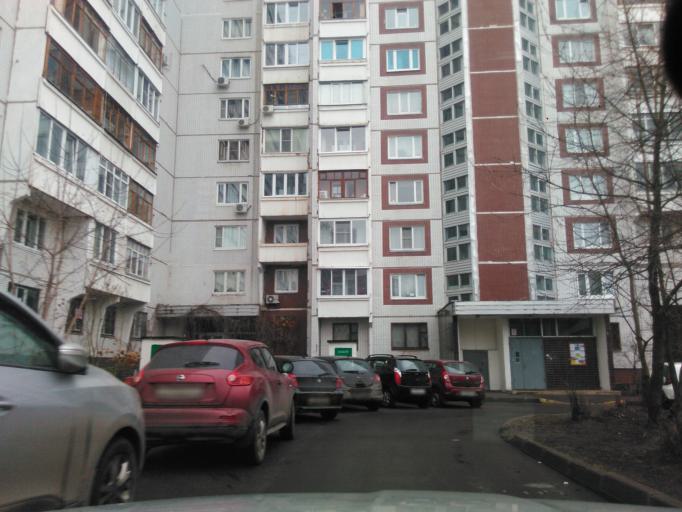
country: RU
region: Moscow
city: Zelenograd
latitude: 55.9719
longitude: 37.1609
